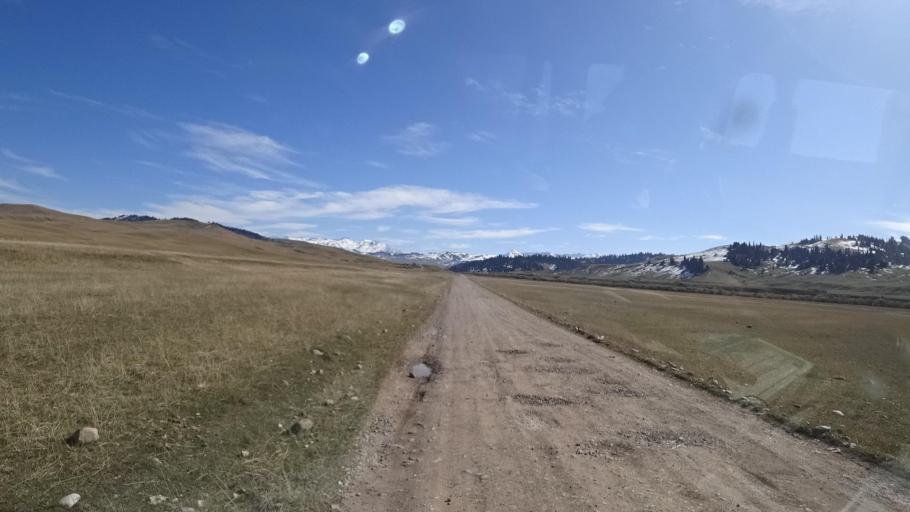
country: KZ
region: Almaty Oblysy
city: Kegen
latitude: 42.7433
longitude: 78.9988
